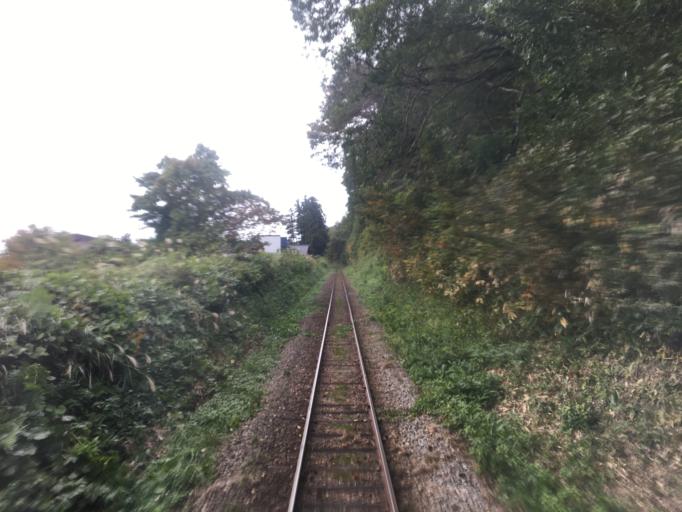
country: JP
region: Yamagata
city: Nagai
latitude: 38.0536
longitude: 140.0755
